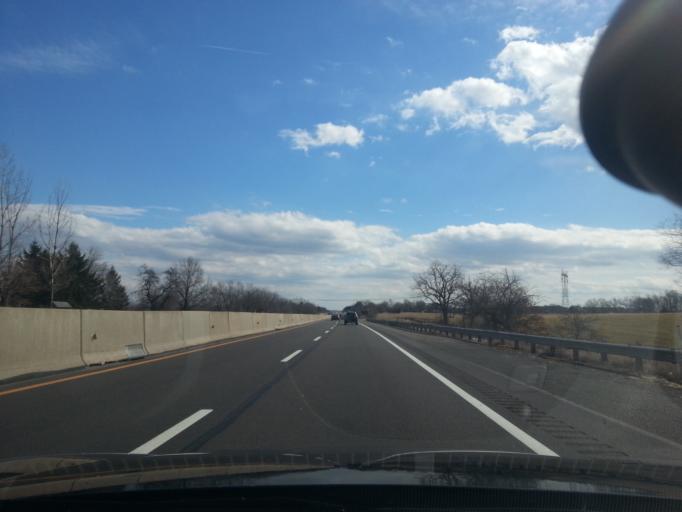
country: US
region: Pennsylvania
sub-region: Montgomery County
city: Harleysville
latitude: 40.2981
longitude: -75.3692
